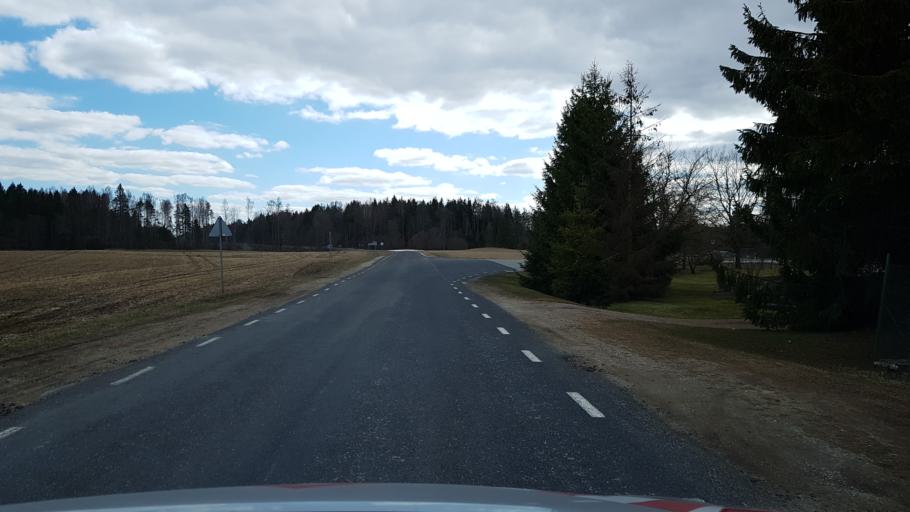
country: EE
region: Laeaene-Virumaa
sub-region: Kadrina vald
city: Kadrina
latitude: 59.2515
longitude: 26.2201
